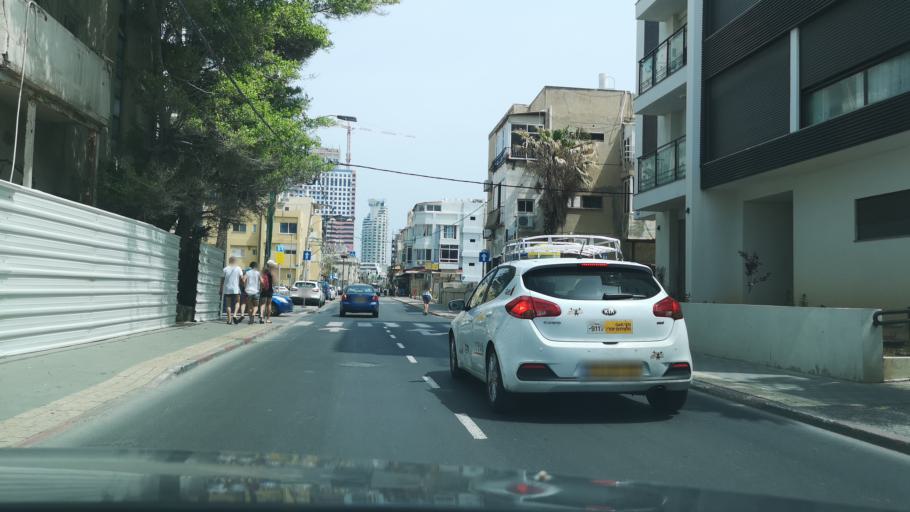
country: IL
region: Tel Aviv
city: Tel Aviv
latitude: 32.0697
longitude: 34.7647
